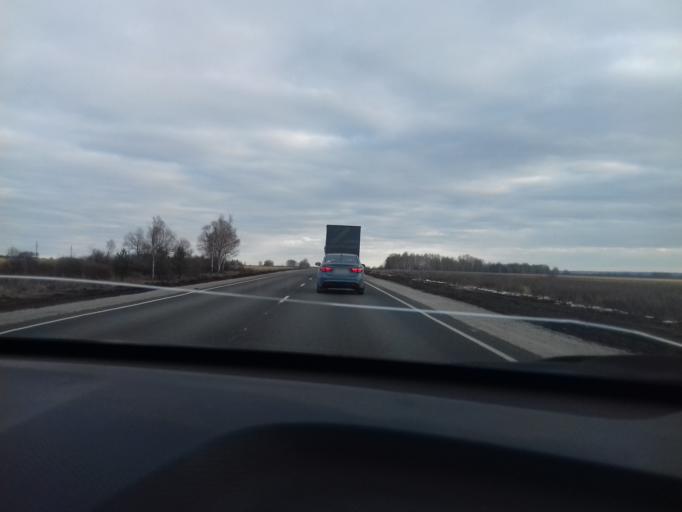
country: RU
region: Kurgan
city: Kataysk
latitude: 56.2929
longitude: 62.6788
